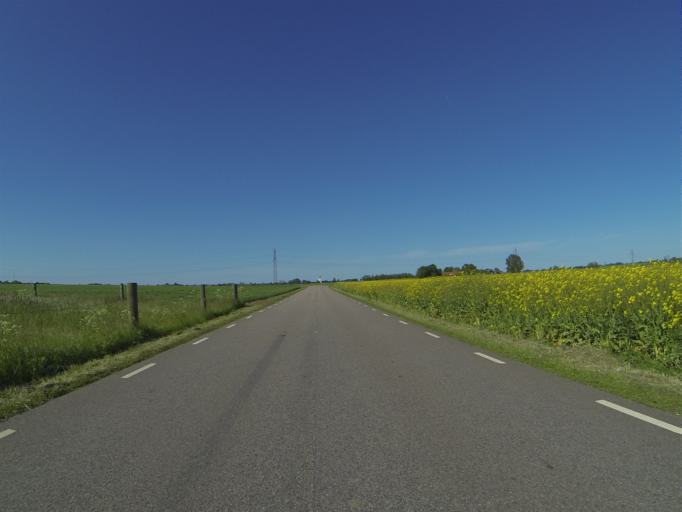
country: SE
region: Skane
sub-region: Staffanstorps Kommun
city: Hjaerup
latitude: 55.6124
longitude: 13.1495
